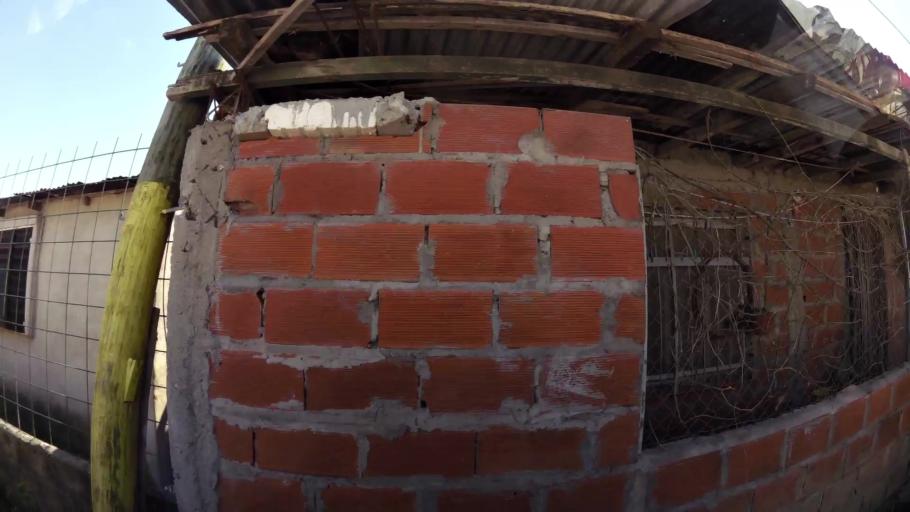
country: AR
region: Buenos Aires
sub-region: Partido de Quilmes
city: Quilmes
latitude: -34.7054
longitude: -58.3023
